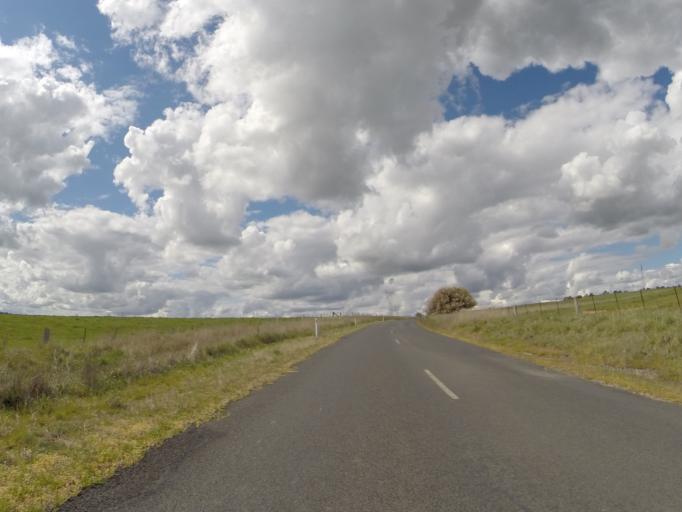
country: AU
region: New South Wales
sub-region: Yass Valley
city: Yass
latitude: -34.8773
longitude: 148.9006
